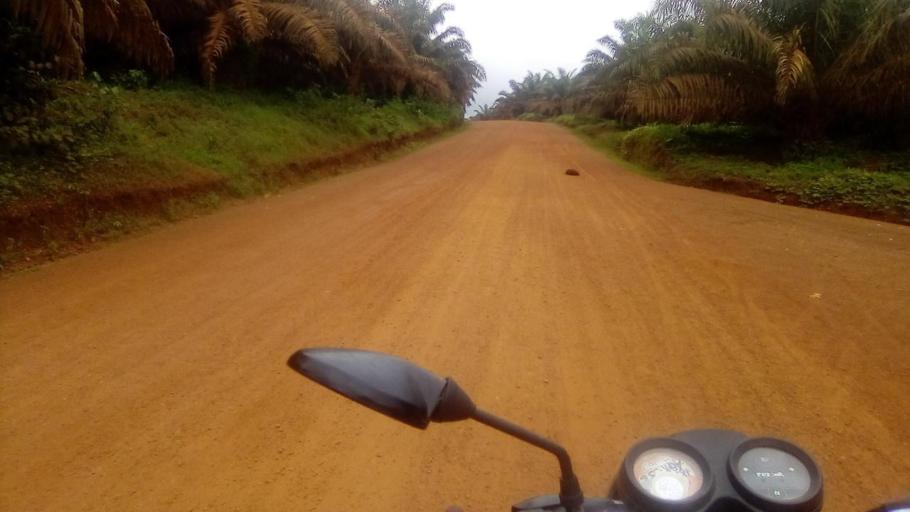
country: SL
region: Southern Province
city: Tongole
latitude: 7.4326
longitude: -11.8491
